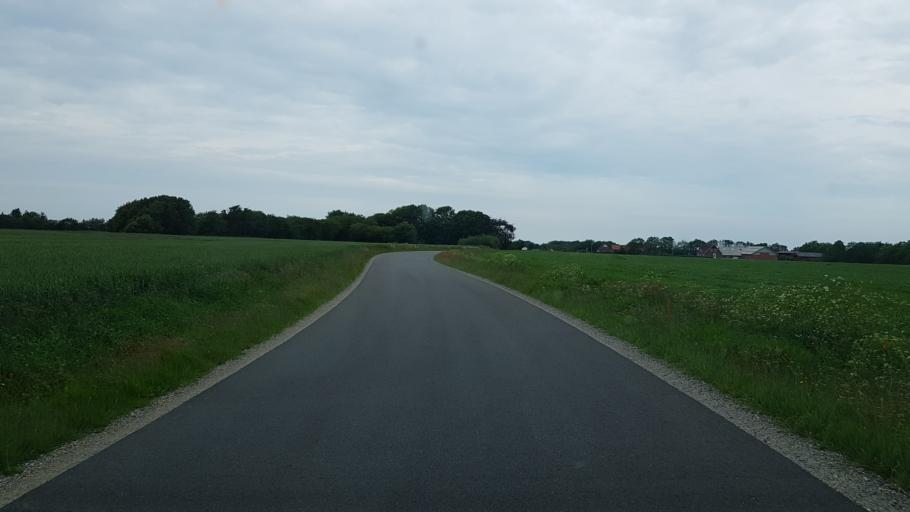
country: DK
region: South Denmark
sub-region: Varde Kommune
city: Oksbol
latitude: 55.7203
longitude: 8.3697
